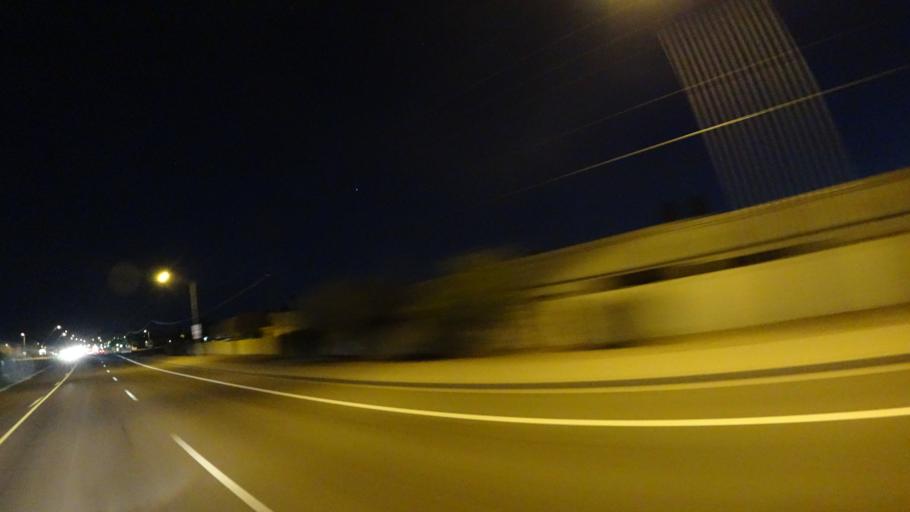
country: US
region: Arizona
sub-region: Maricopa County
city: Mesa
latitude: 33.4518
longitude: -111.6914
